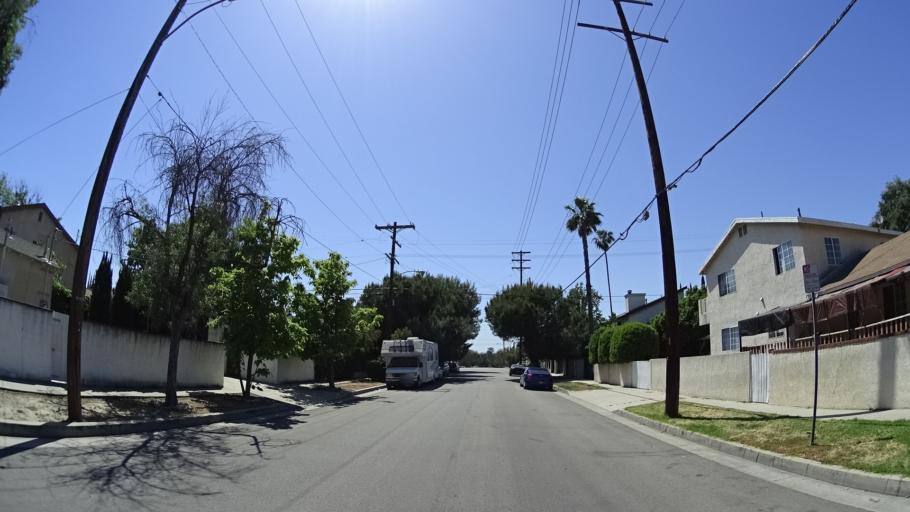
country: US
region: California
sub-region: Los Angeles County
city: North Hollywood
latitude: 34.1758
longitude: -118.3868
